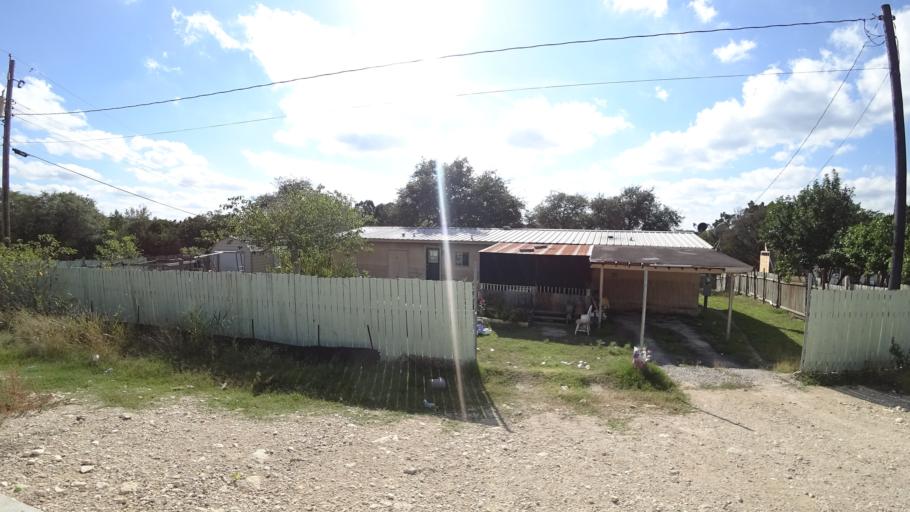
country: US
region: Texas
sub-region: Travis County
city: Barton Creek
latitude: 30.2454
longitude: -97.8789
